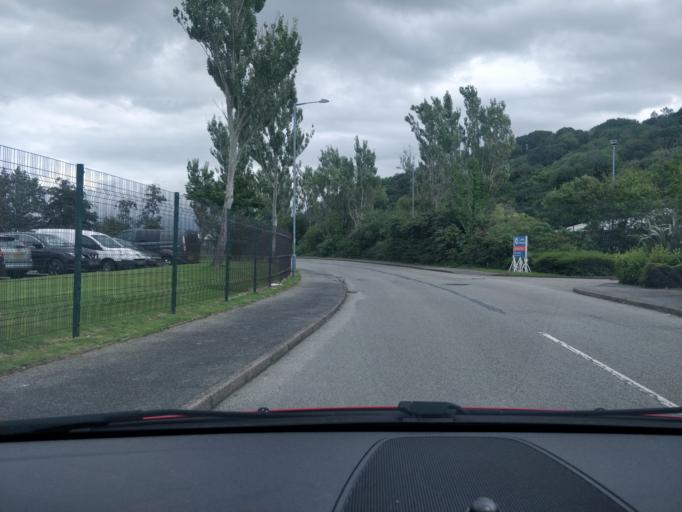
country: GB
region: Wales
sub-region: Gwynedd
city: Porthmadog
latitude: 52.9310
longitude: -4.1441
